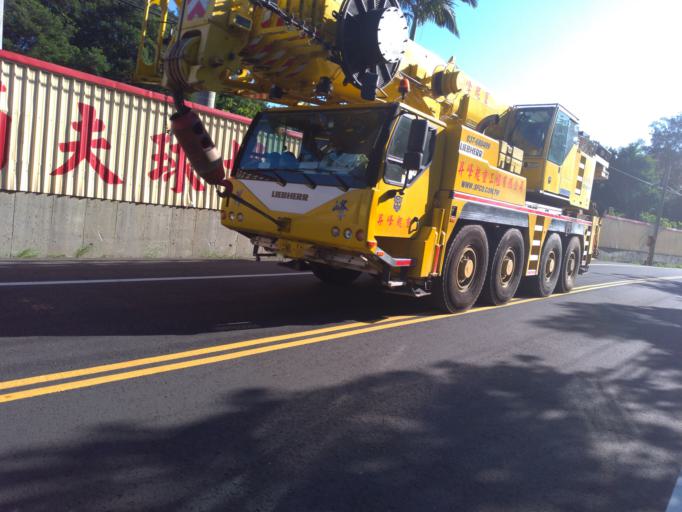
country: TW
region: Taiwan
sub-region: Hsinchu
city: Hsinchu
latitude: 24.7349
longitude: 120.9684
